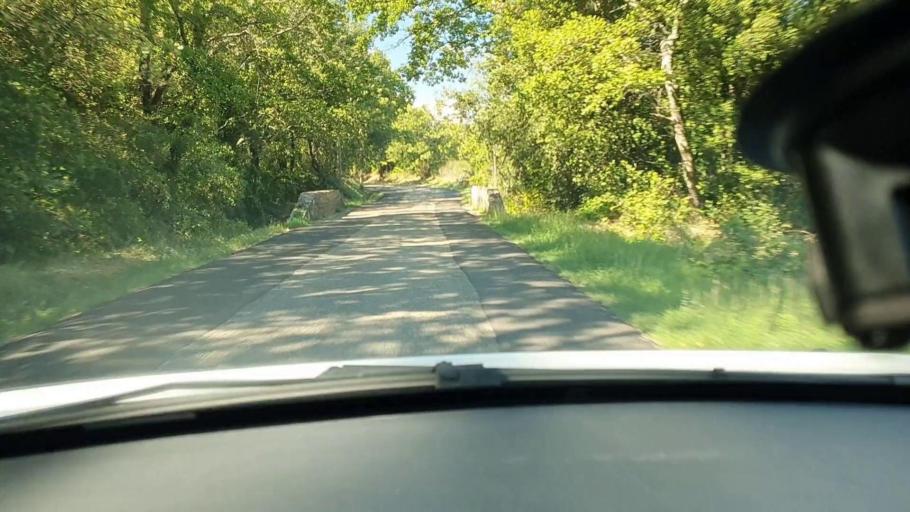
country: FR
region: Languedoc-Roussillon
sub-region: Departement du Gard
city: Sabran
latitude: 44.1748
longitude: 4.5128
